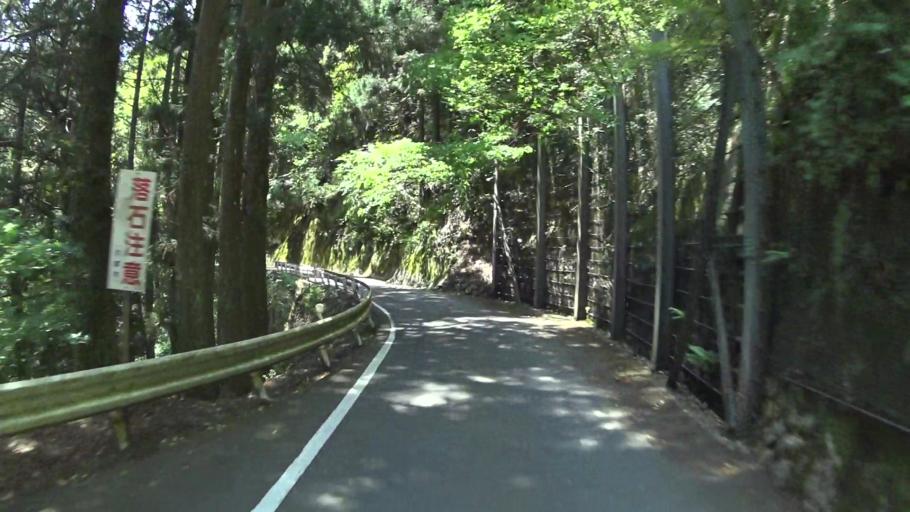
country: JP
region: Kyoto
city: Kameoka
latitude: 35.1325
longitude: 135.5840
